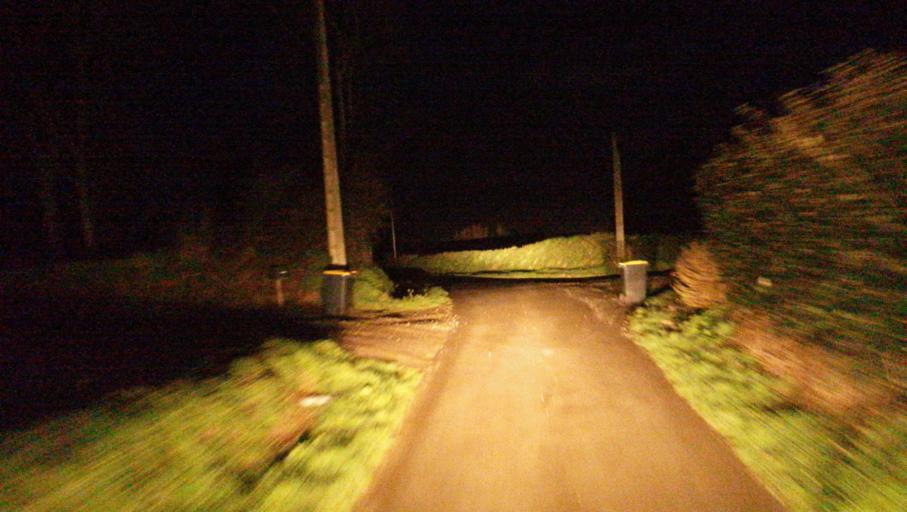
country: FR
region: Brittany
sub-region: Departement des Cotes-d'Armor
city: Plehedel
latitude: 48.6799
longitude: -3.0319
